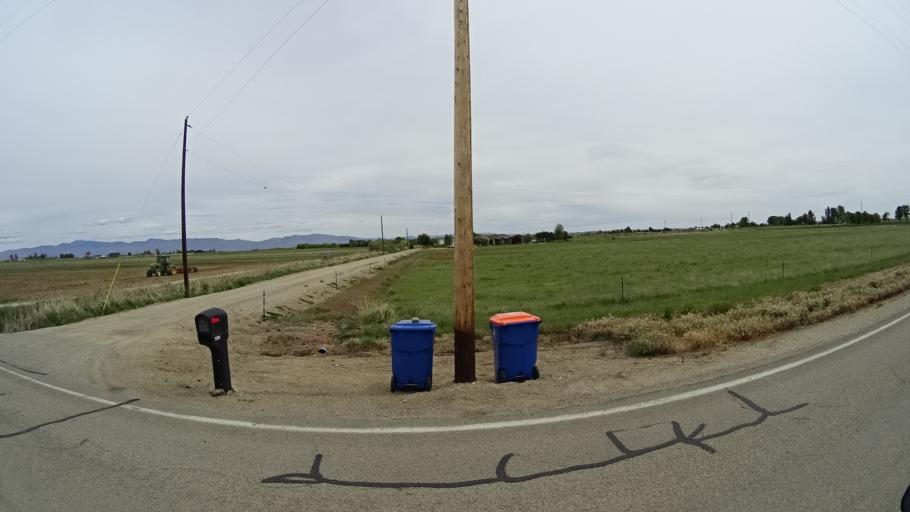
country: US
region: Idaho
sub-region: Ada County
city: Kuna
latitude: 43.5391
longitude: -116.3749
